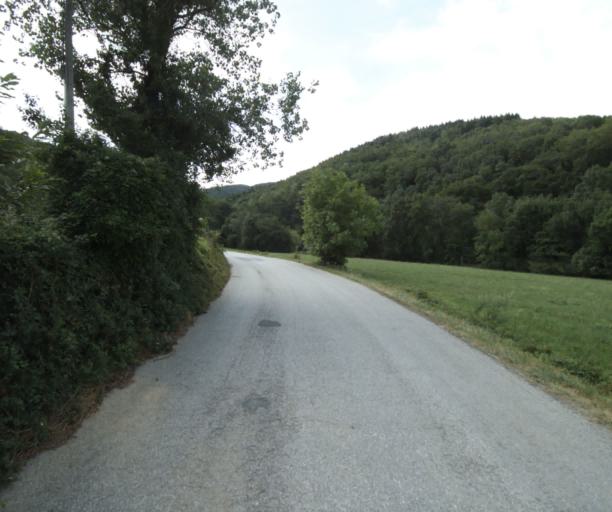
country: FR
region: Midi-Pyrenees
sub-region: Departement du Tarn
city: Soreze
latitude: 43.4629
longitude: 2.1035
